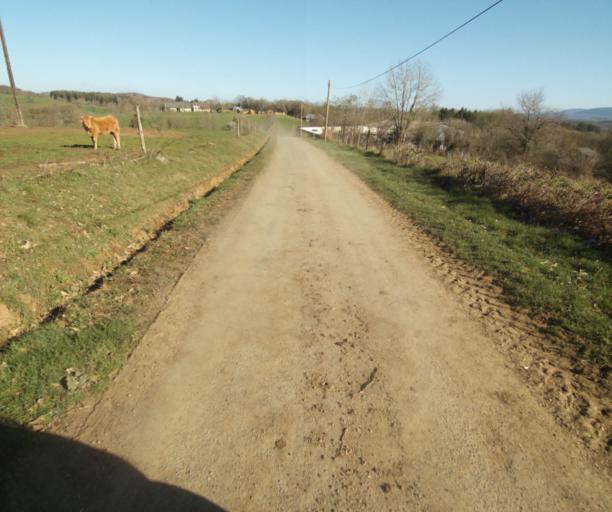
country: FR
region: Limousin
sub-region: Departement de la Correze
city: Seilhac
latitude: 45.3787
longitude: 1.7643
